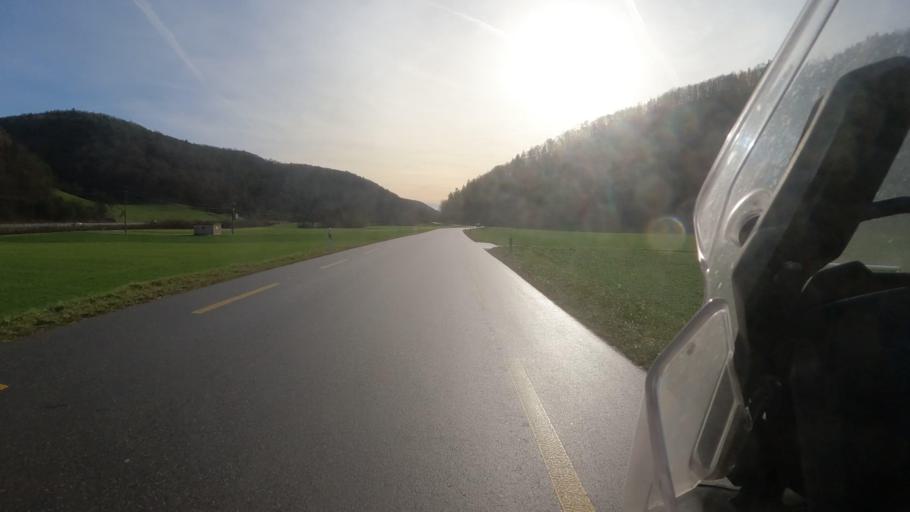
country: CH
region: Schaffhausen
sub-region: Bezirk Reiat
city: Stetten
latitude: 47.7530
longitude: 8.6139
